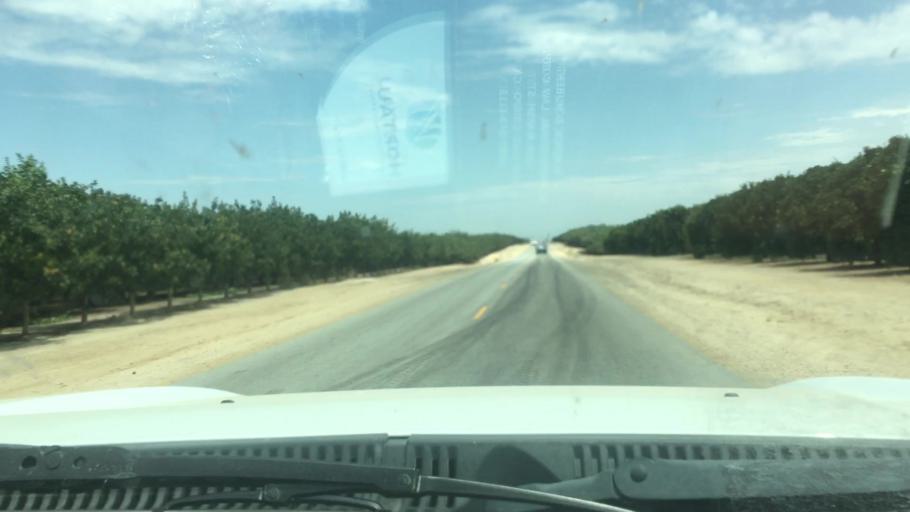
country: US
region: California
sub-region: Kern County
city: McFarland
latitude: 35.5806
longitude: -119.1511
